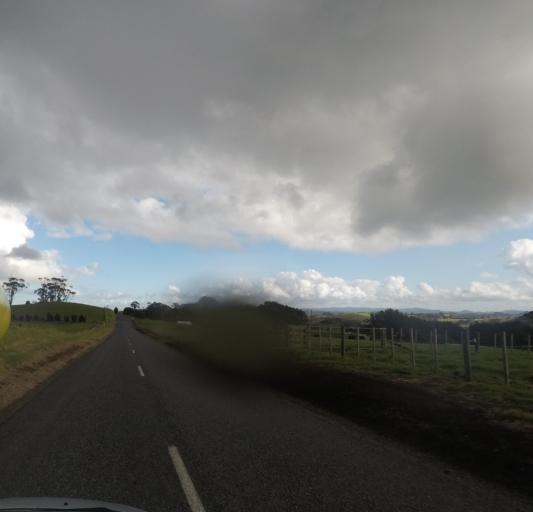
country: NZ
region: Auckland
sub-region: Auckland
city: Warkworth
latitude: -36.3692
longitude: 174.7659
